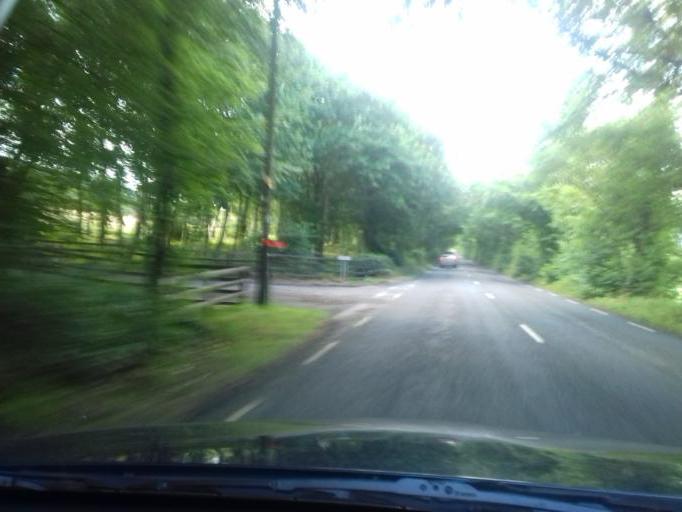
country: IE
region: Leinster
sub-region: Kilkenny
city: Graiguenamanagh
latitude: 52.4768
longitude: -6.9510
